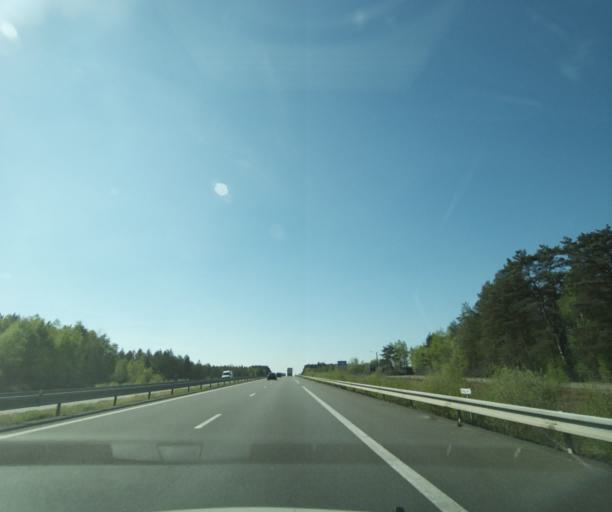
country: FR
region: Centre
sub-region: Departement du Loir-et-Cher
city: Theillay
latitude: 47.3637
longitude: 2.0529
